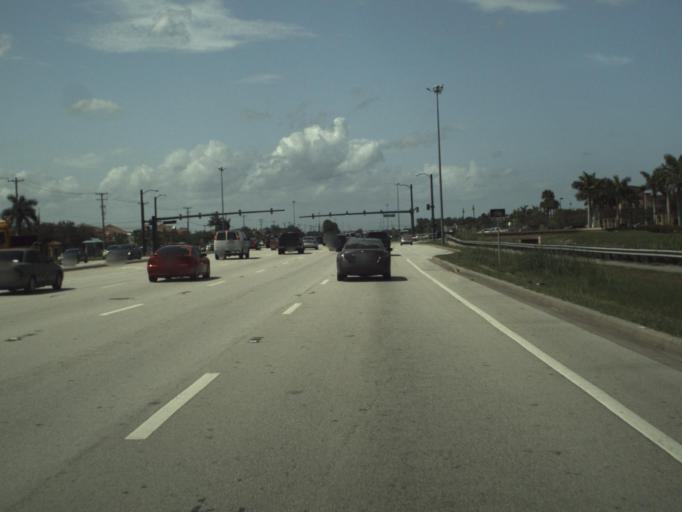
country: US
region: Florida
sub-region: Palm Beach County
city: Wellington
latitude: 26.6634
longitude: -80.2028
